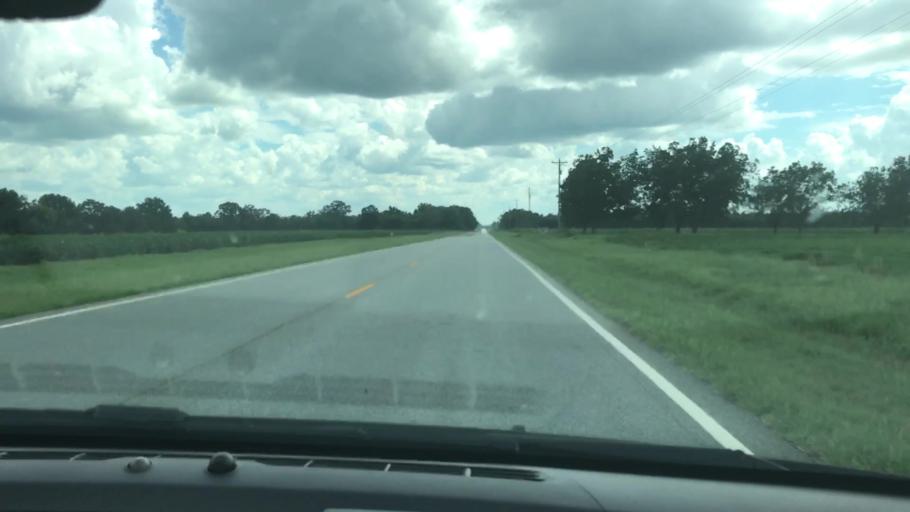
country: US
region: Georgia
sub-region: Quitman County
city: Georgetown
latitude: 31.8070
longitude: -85.0932
